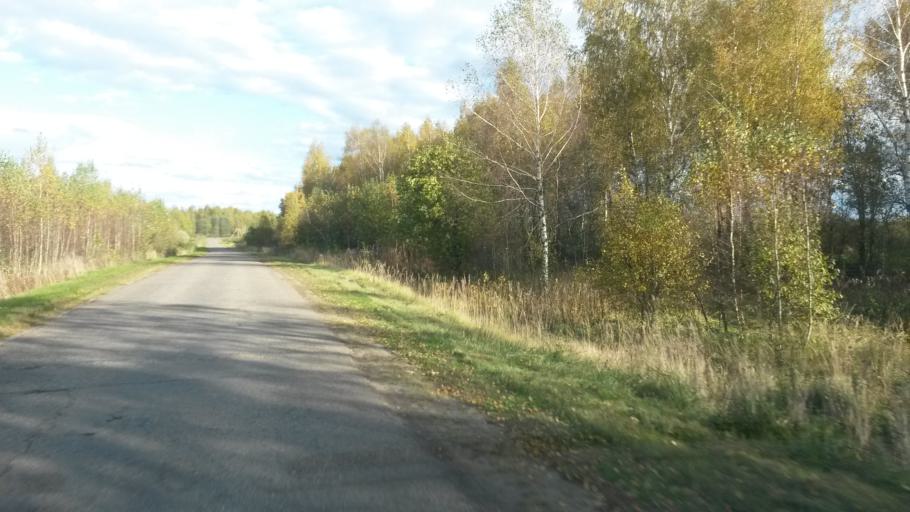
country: RU
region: Jaroslavl
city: Tunoshna
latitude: 57.5256
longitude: 39.9930
